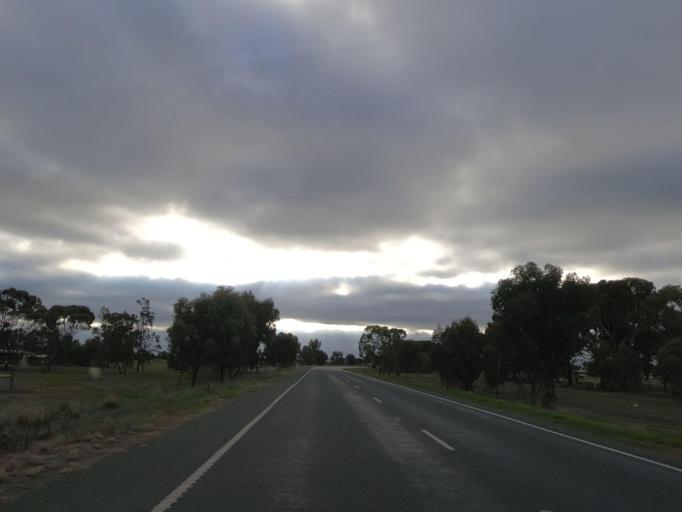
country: AU
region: Victoria
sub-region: Swan Hill
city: Swan Hill
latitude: -35.7306
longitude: 143.8942
